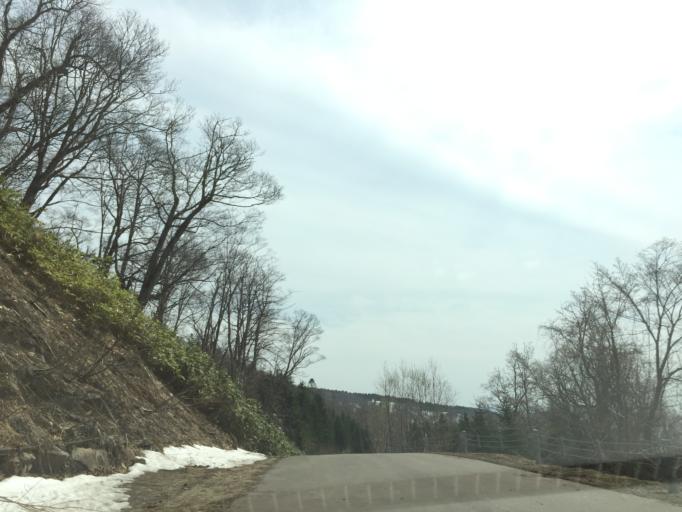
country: JP
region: Hokkaido
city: Akabira
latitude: 43.6043
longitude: 142.0667
